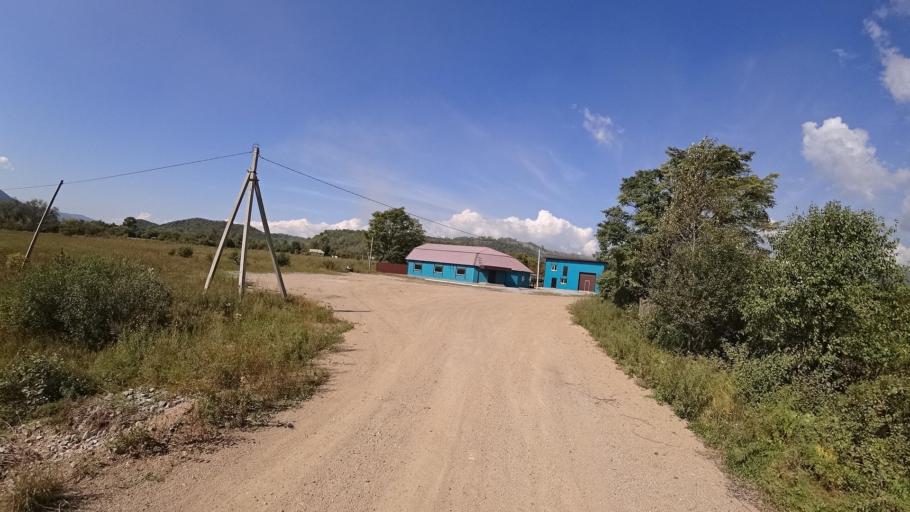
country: RU
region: Jewish Autonomous Oblast
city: Londoko
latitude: 49.0032
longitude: 131.9449
